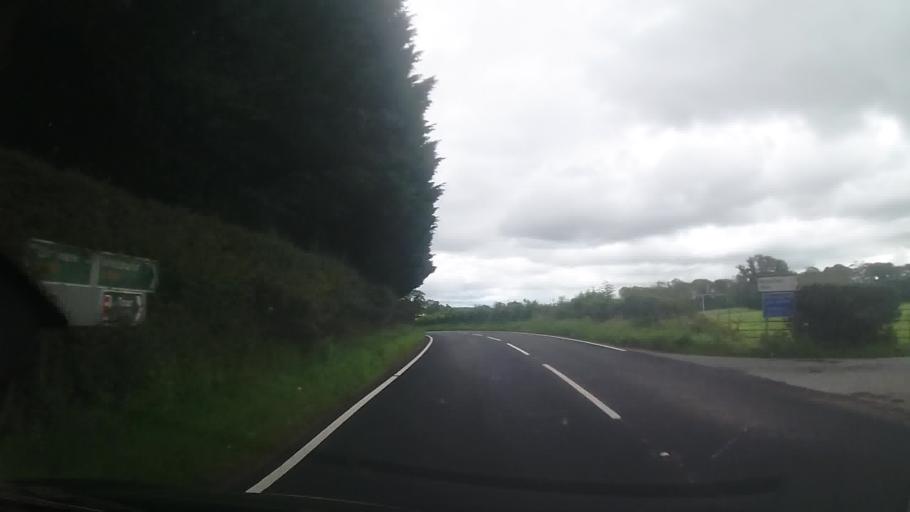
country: GB
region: England
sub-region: Shropshire
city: Ellesmere
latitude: 52.9292
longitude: -2.8035
